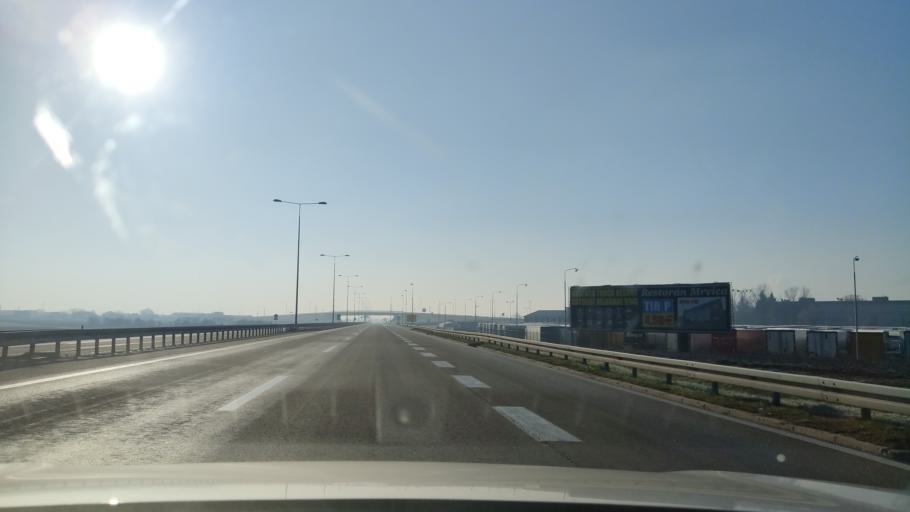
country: RS
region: Central Serbia
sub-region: Belgrade
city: Surcin
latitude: 44.8082
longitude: 20.2538
